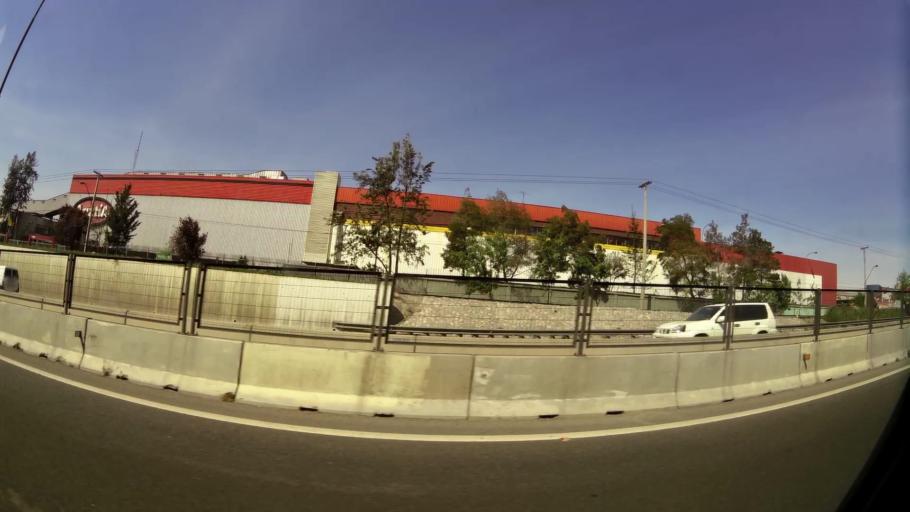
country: CL
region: Santiago Metropolitan
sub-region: Provincia de Santiago
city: Santiago
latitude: -33.5232
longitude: -70.6772
